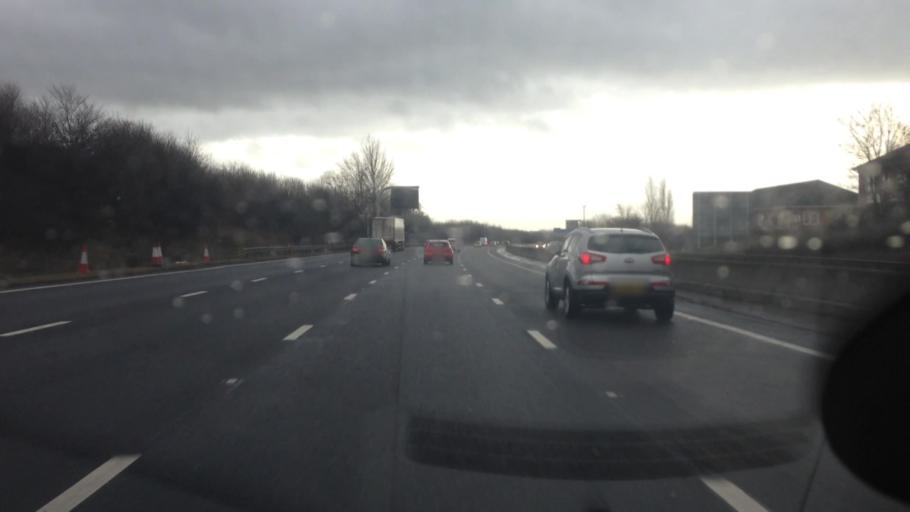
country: GB
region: England
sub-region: City and Borough of Wakefield
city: Horbury
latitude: 53.6674
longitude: -1.5415
